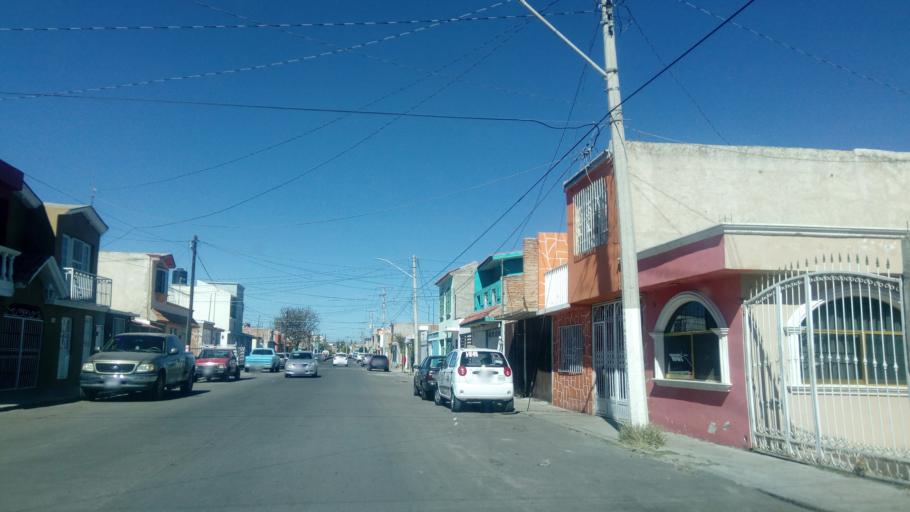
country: MX
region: Durango
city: Victoria de Durango
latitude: 24.0175
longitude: -104.6409
